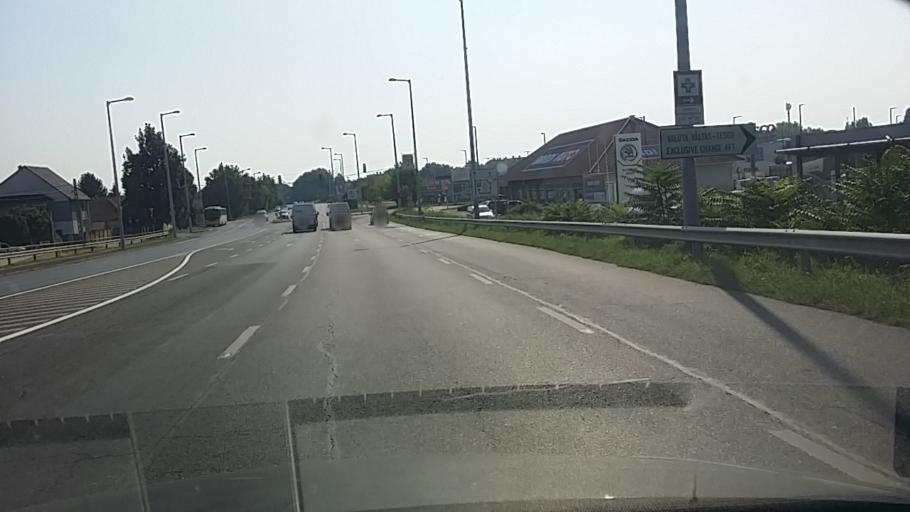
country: HU
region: Bekes
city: Bekescsaba
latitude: 46.6820
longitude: 21.0714
